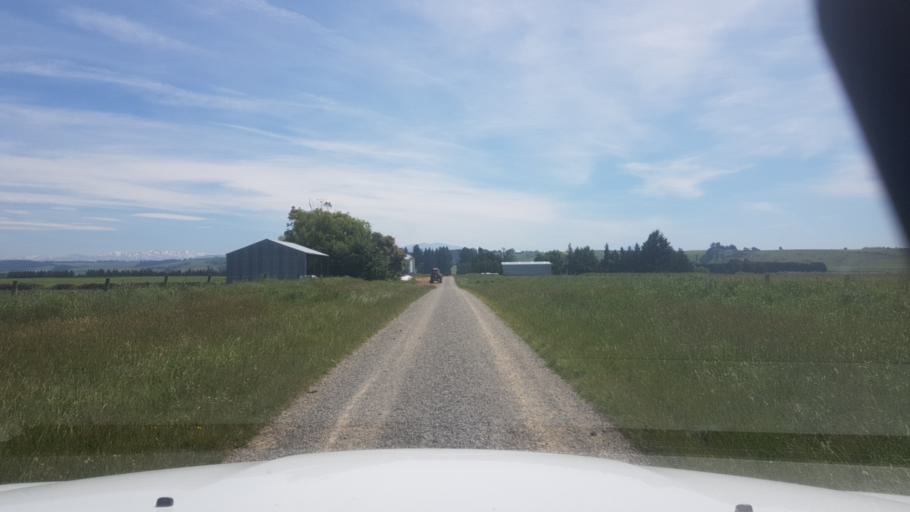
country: NZ
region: Canterbury
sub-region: Timaru District
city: Pleasant Point
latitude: -44.2268
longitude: 171.1650
